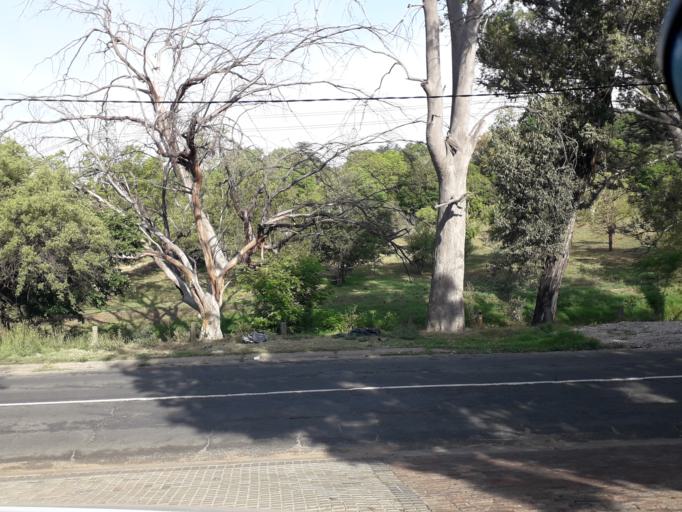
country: ZA
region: Gauteng
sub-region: City of Johannesburg Metropolitan Municipality
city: Midrand
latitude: -26.0630
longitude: 28.0417
